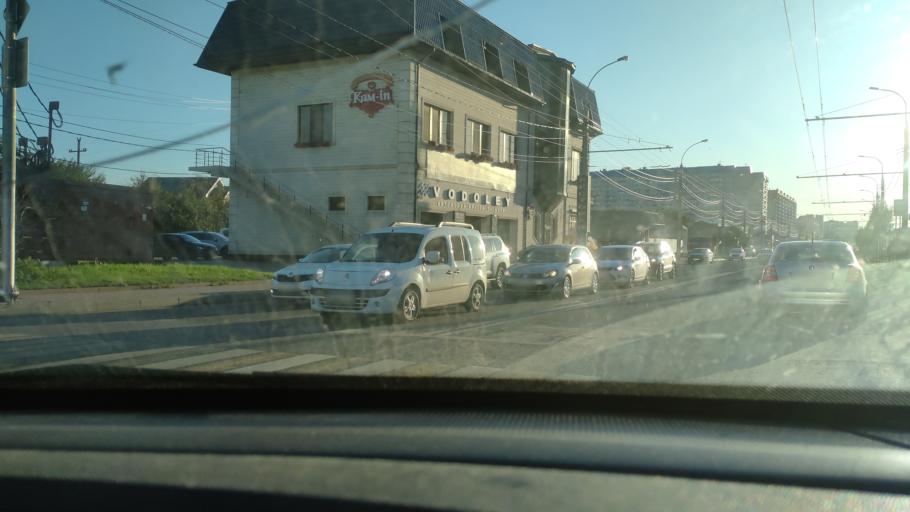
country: RU
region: Adygeya
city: Yablonovskiy
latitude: 45.0360
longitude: 38.9257
